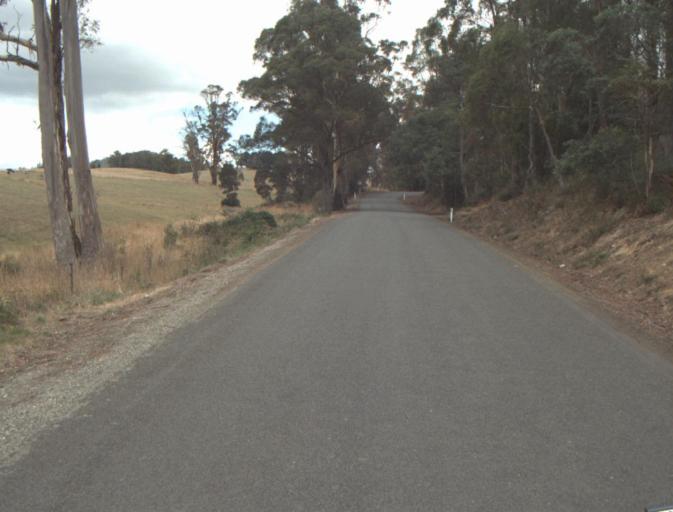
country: AU
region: Tasmania
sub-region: Launceston
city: Mayfield
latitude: -41.2380
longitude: 147.1970
